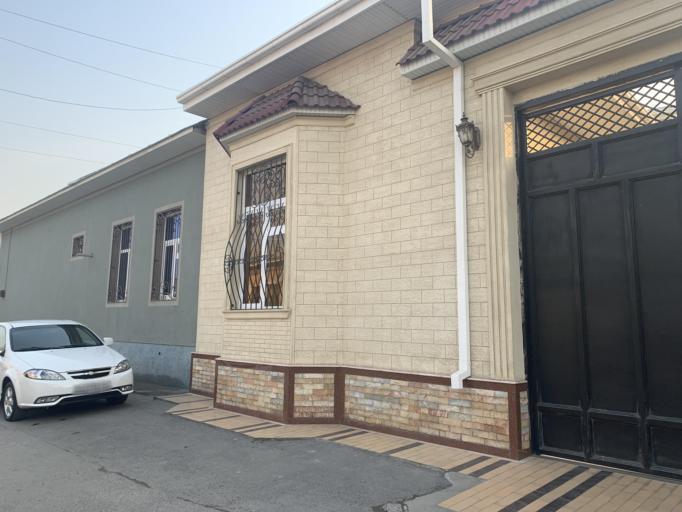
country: UZ
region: Fergana
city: Qo`qon
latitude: 40.5377
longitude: 70.9301
